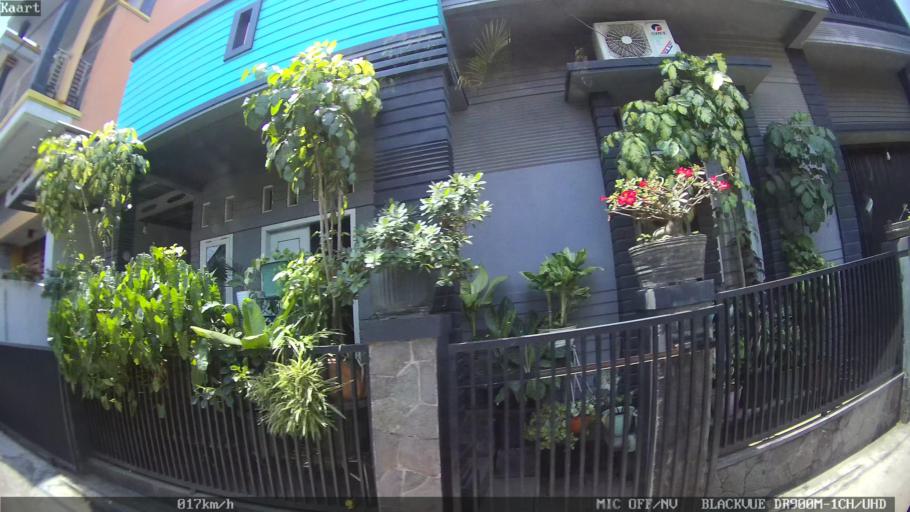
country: ID
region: Lampung
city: Kedaton
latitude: -5.3915
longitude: 105.2679
